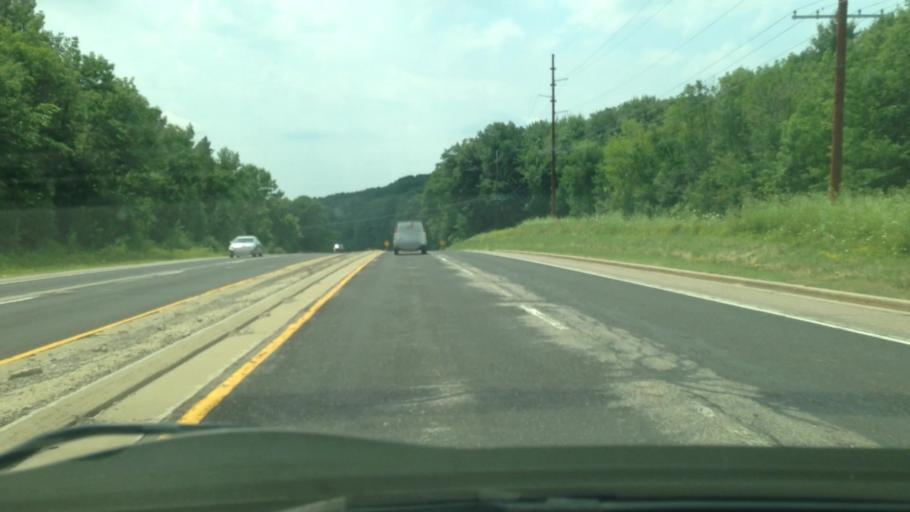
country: US
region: Wisconsin
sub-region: Sauk County
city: West Baraboo
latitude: 43.4008
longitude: -89.7726
